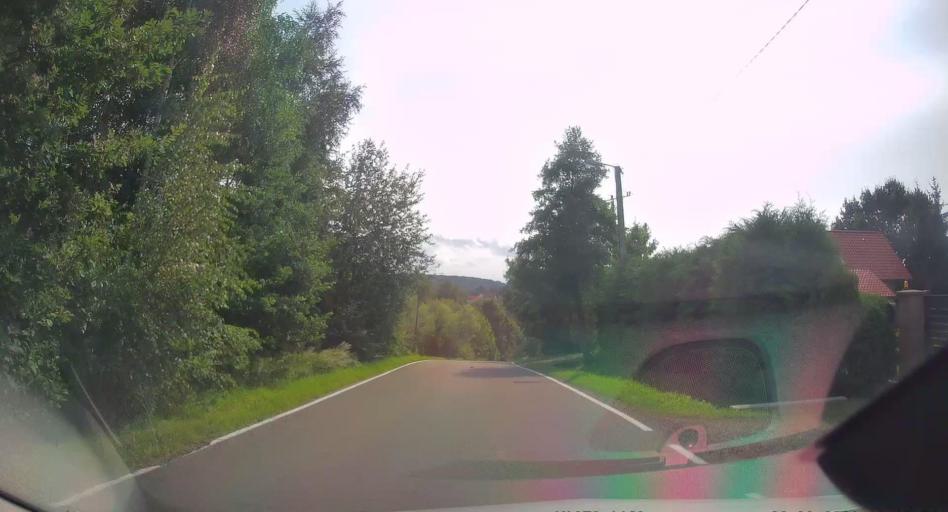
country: PL
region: Lesser Poland Voivodeship
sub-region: Powiat wielicki
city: Pawlikowice
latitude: 49.9547
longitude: 20.0439
